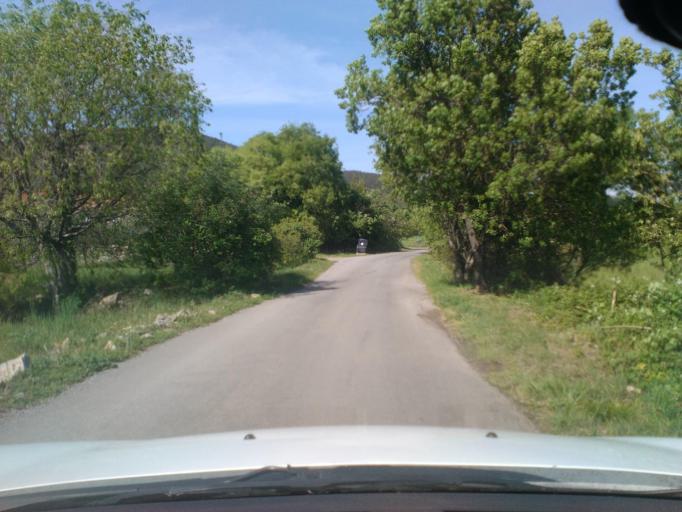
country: FR
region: Languedoc-Roussillon
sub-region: Departement du Gard
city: Saint-Hippolyte-du-Fort
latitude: 43.9981
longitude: 3.8876
